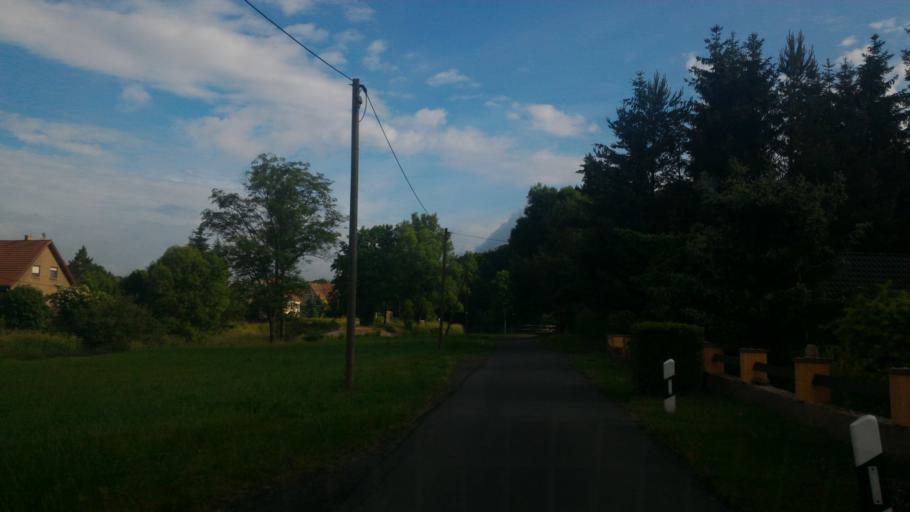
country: DE
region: Saxony
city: Mittelherwigsdorf
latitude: 50.9195
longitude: 14.7469
